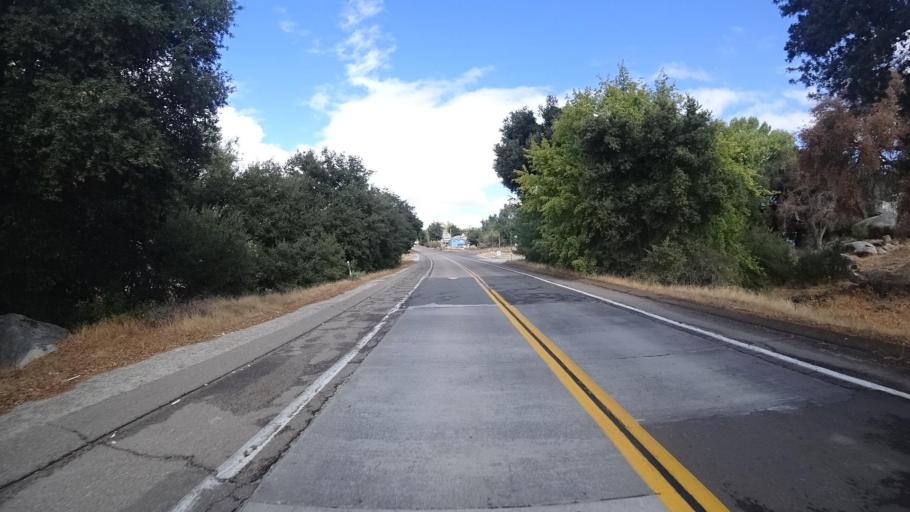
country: US
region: California
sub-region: San Diego County
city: Campo
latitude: 32.6862
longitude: -116.3357
